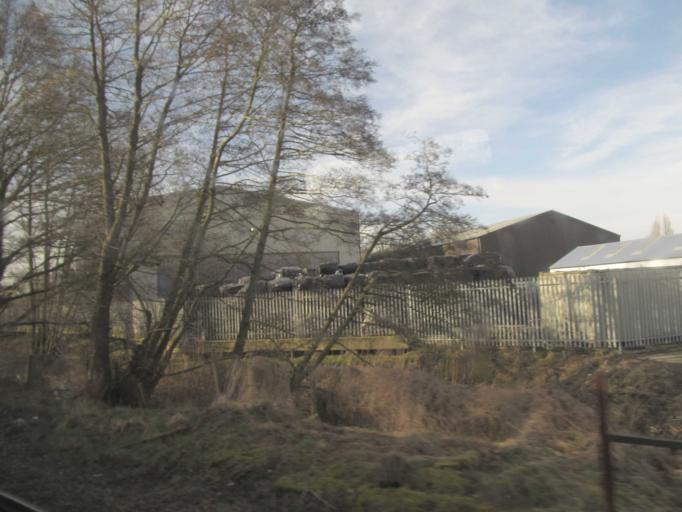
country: GB
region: England
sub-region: Hampshire
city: Farnborough
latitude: 51.2792
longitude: -0.7327
